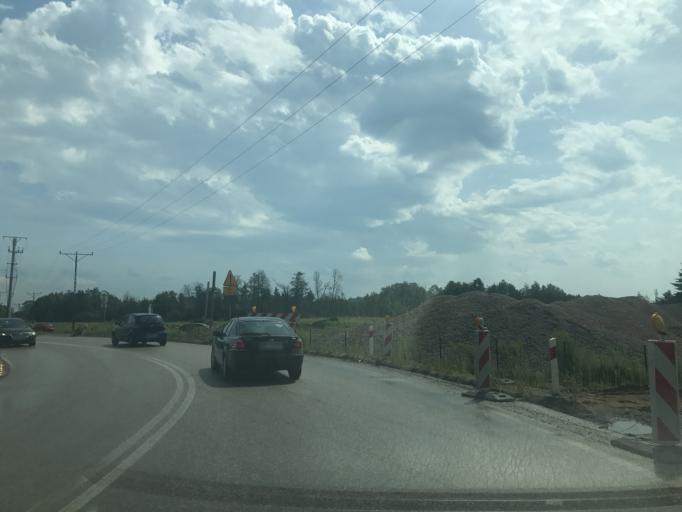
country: PL
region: Warmian-Masurian Voivodeship
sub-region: Powiat ostrodzki
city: Ostroda
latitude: 53.7147
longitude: 19.9601
